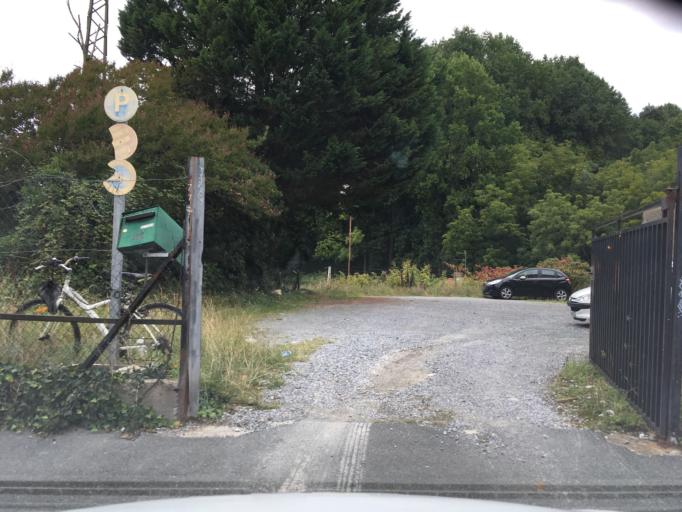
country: FR
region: Aquitaine
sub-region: Departement des Pyrenees-Atlantiques
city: Bayonne
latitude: 43.4980
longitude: -1.4676
